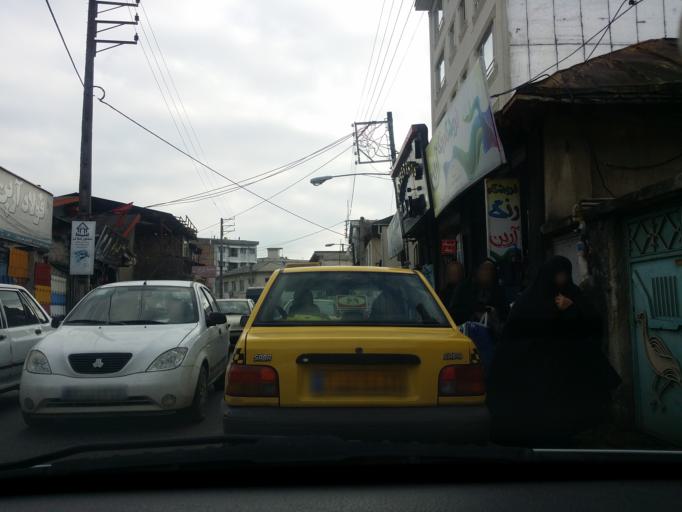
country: IR
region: Mazandaran
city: Chalus
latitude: 36.6569
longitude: 51.4133
